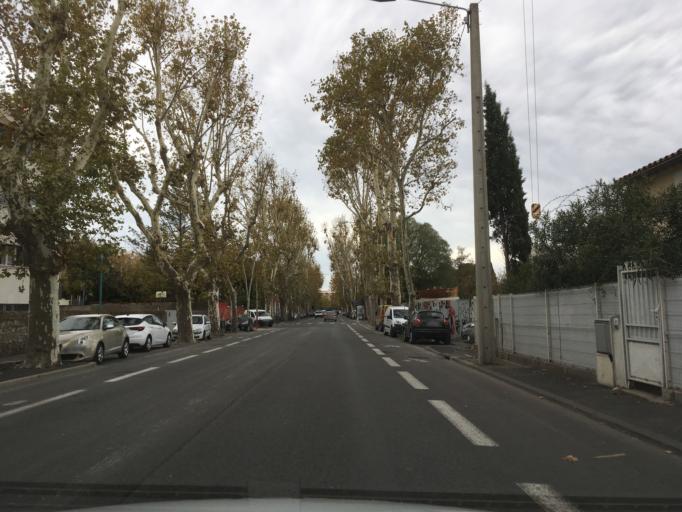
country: FR
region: Languedoc-Roussillon
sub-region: Departement de l'Herault
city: Montpellier
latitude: 43.6199
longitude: 3.8869
